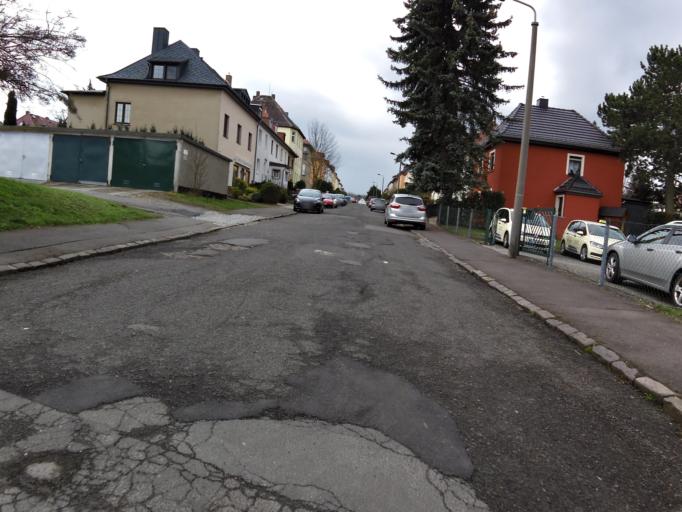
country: DE
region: Saxony
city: Markkleeberg
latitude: 51.2866
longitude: 12.4061
